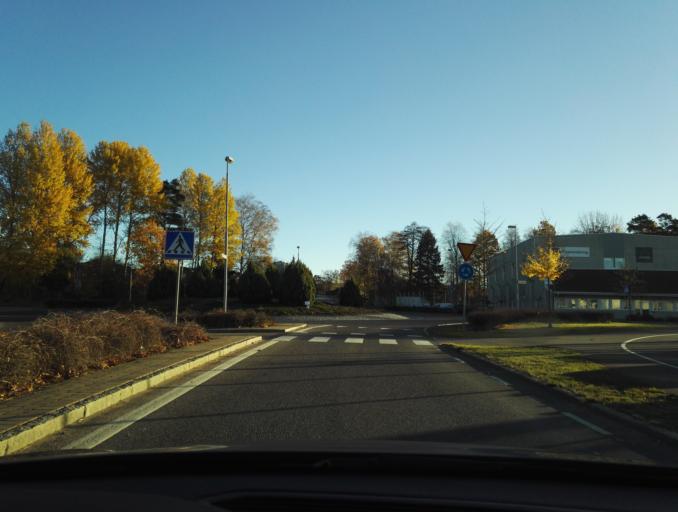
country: SE
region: Kronoberg
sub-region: Vaxjo Kommun
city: Vaexjoe
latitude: 56.8950
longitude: 14.7808
